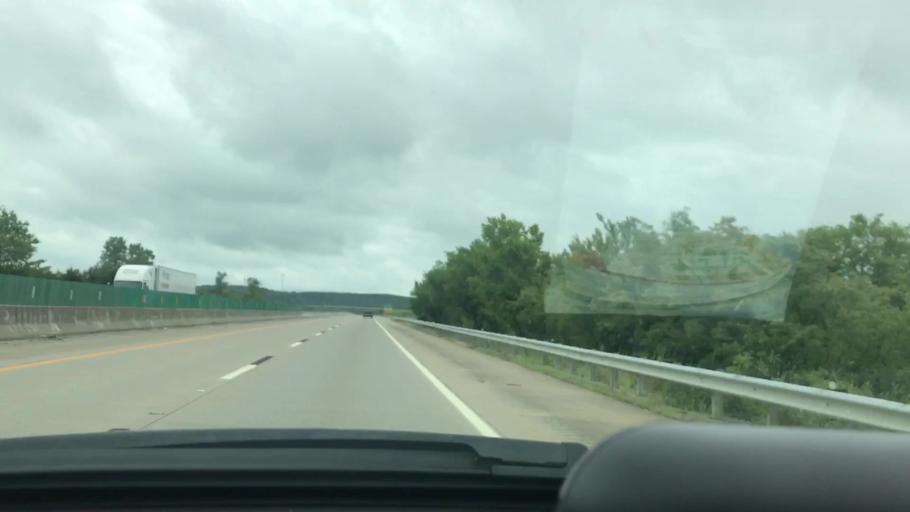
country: US
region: Oklahoma
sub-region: Pittsburg County
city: Krebs
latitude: 35.0960
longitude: -95.6988
